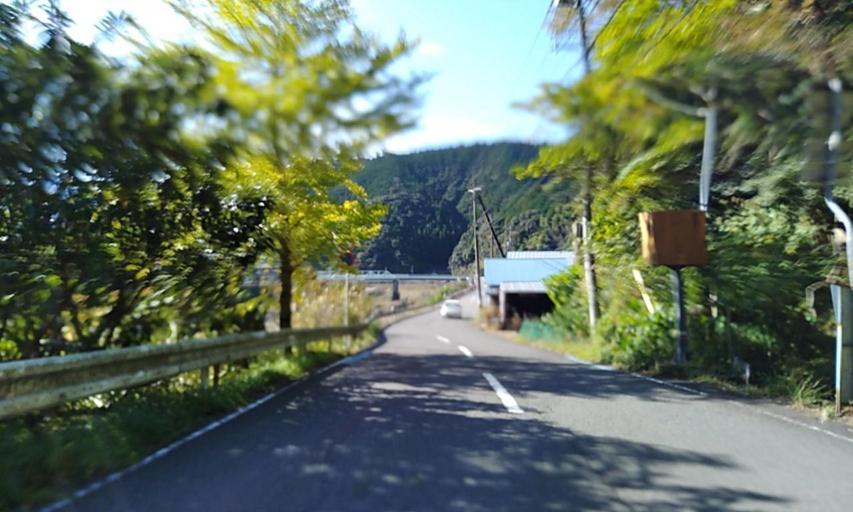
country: JP
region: Wakayama
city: Kainan
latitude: 34.0733
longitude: 135.3576
